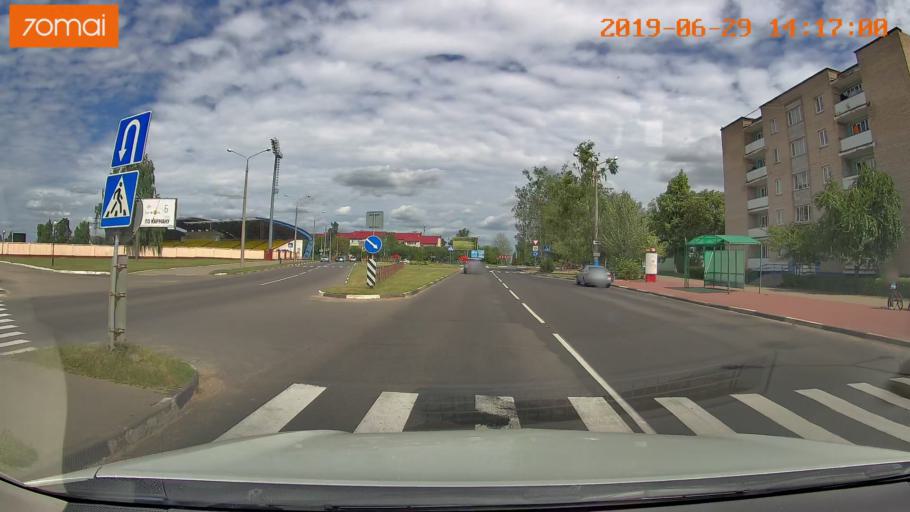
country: BY
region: Minsk
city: Salihorsk
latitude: 52.7971
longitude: 27.5375
